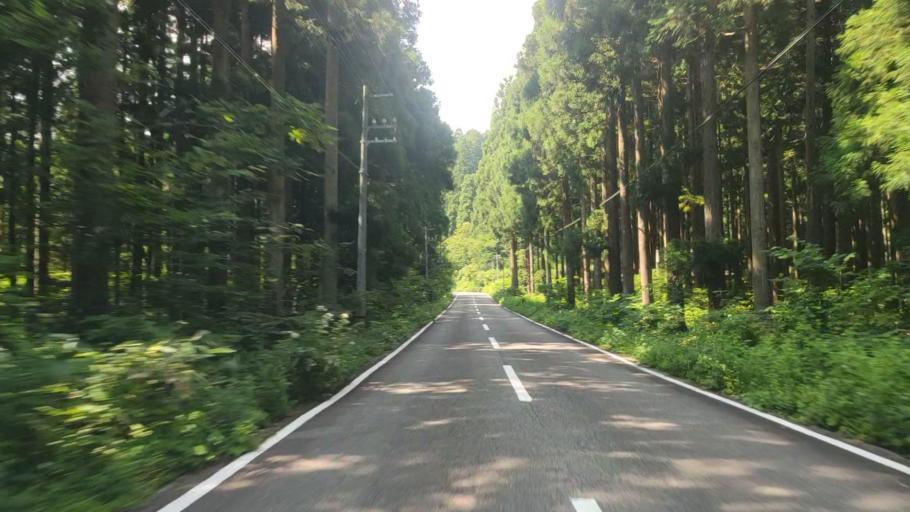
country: JP
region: Fukui
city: Katsuyama
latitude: 36.2324
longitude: 136.5306
